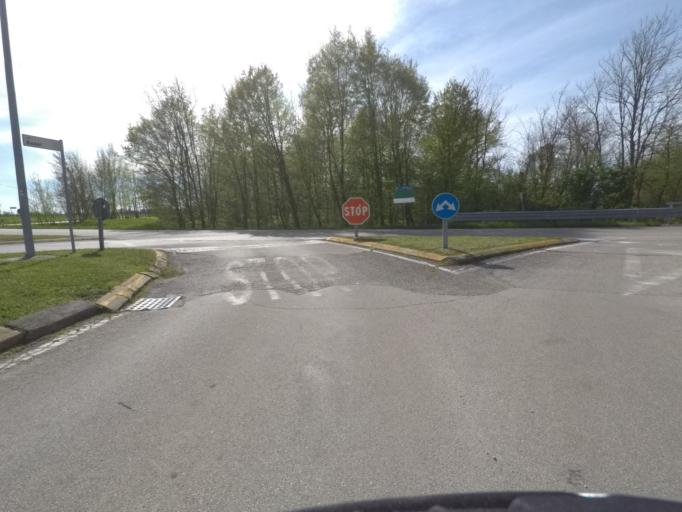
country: IT
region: Friuli Venezia Giulia
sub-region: Provincia di Pordenone
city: Fiume Veneto
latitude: 45.9362
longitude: 12.7032
